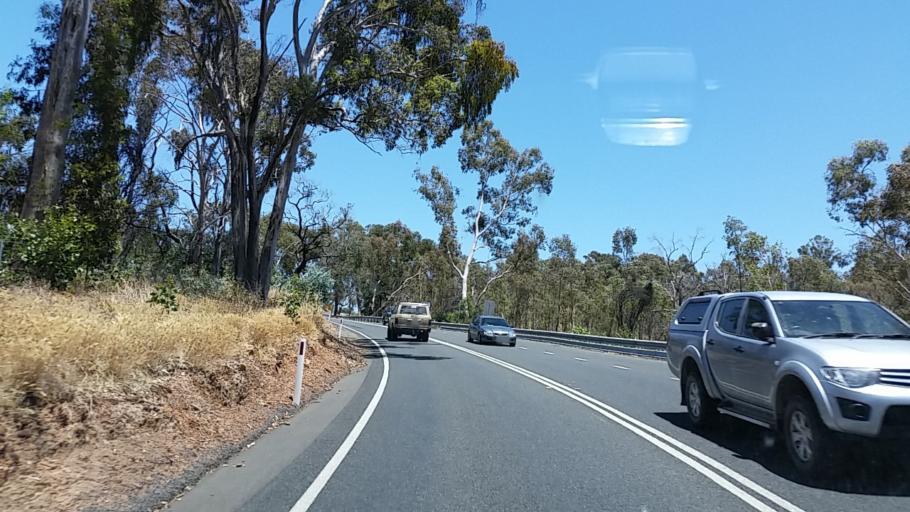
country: AU
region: South Australia
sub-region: Adelaide Hills
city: Gumeracha
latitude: -34.8149
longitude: 138.8089
